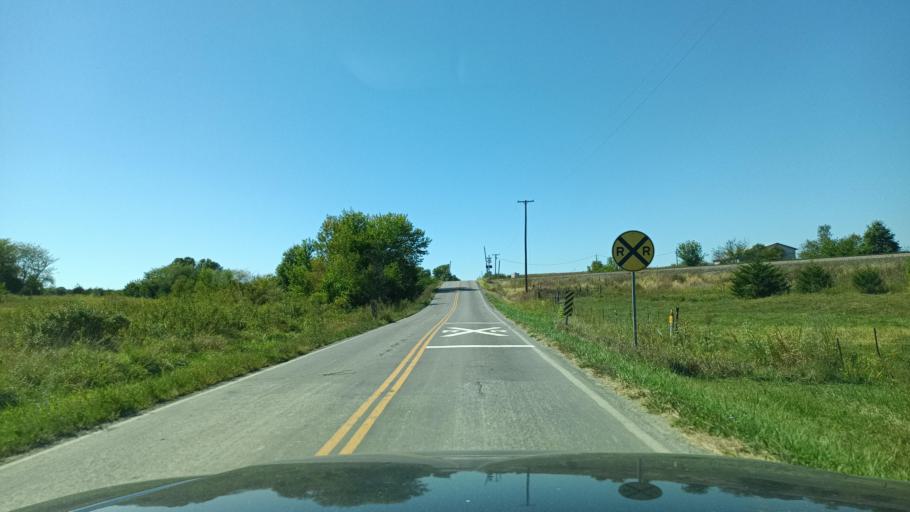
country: US
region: Missouri
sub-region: Macon County
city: La Plata
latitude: 40.0215
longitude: -92.5128
